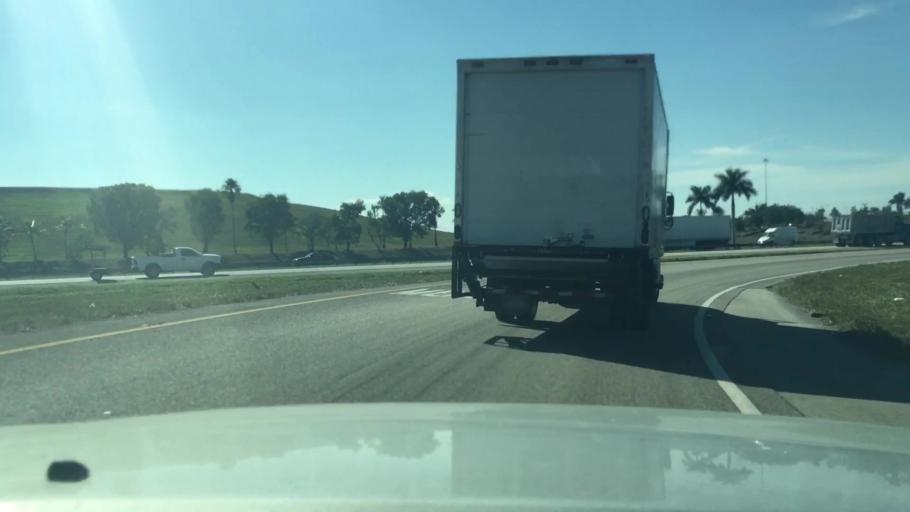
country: US
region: Florida
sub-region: Miami-Dade County
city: Country Club
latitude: 25.9713
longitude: -80.2939
